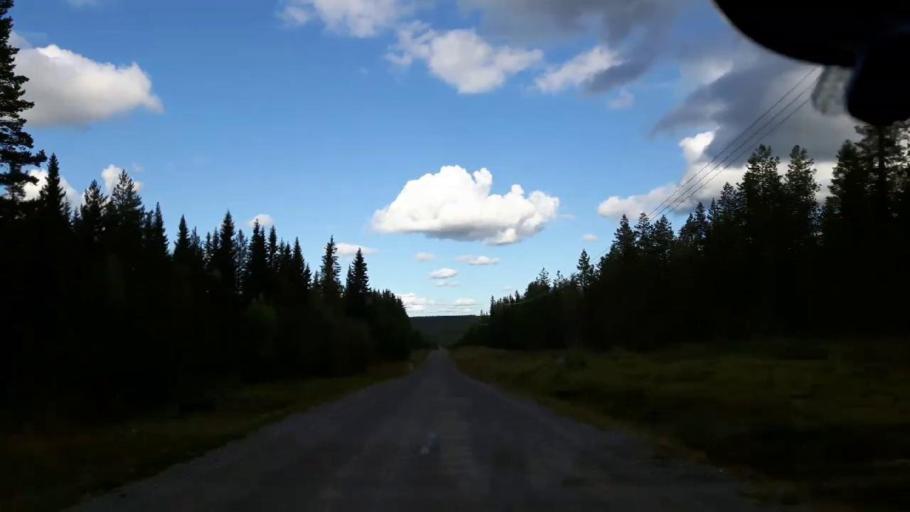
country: SE
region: Jaemtland
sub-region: Stroemsunds Kommun
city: Stroemsund
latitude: 63.4113
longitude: 15.7812
